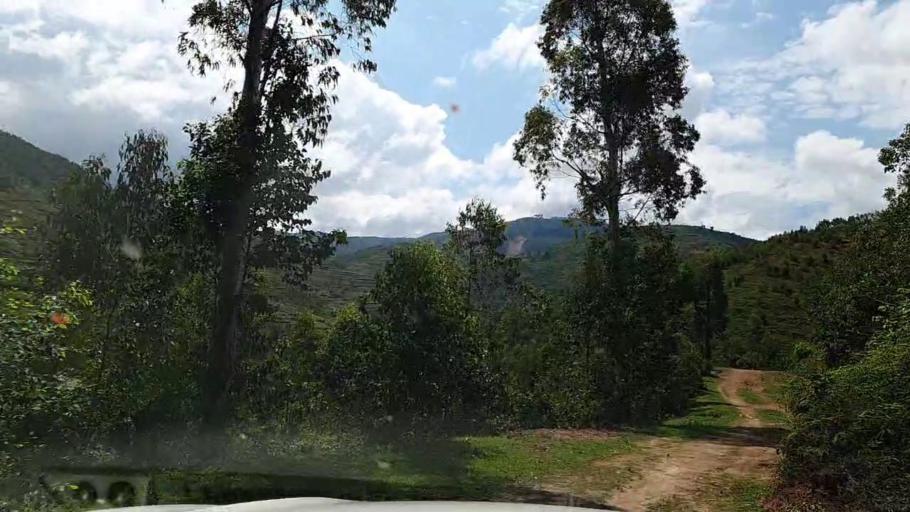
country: RW
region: Southern Province
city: Gikongoro
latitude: -2.3613
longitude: 29.5367
